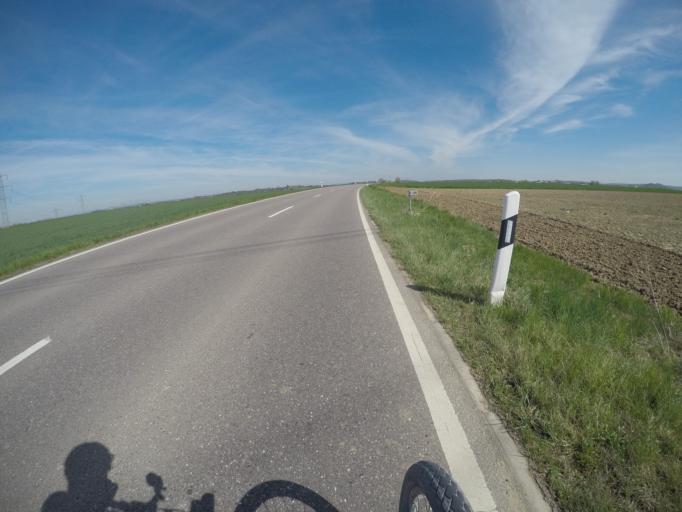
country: DE
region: Baden-Wuerttemberg
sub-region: Regierungsbezirk Stuttgart
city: Schwieberdingen
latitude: 48.8570
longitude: 9.0739
